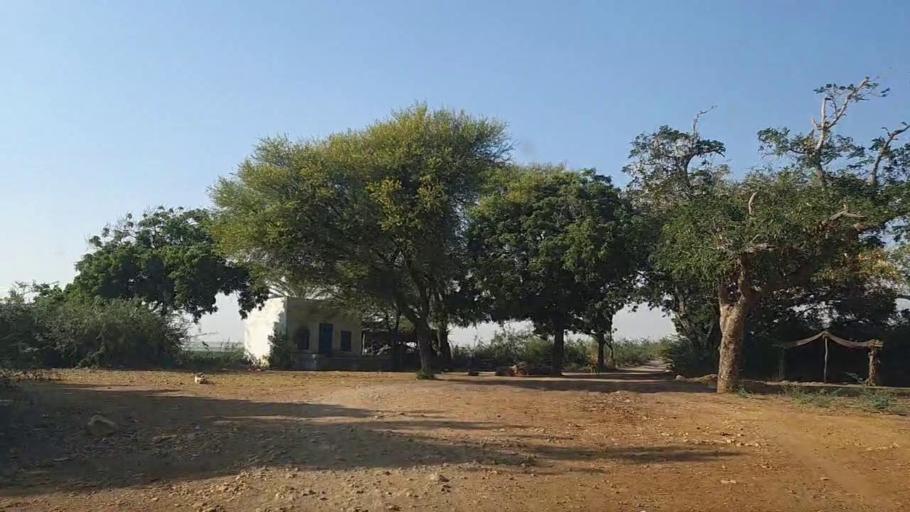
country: PK
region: Sindh
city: Daro Mehar
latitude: 25.0396
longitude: 68.1365
